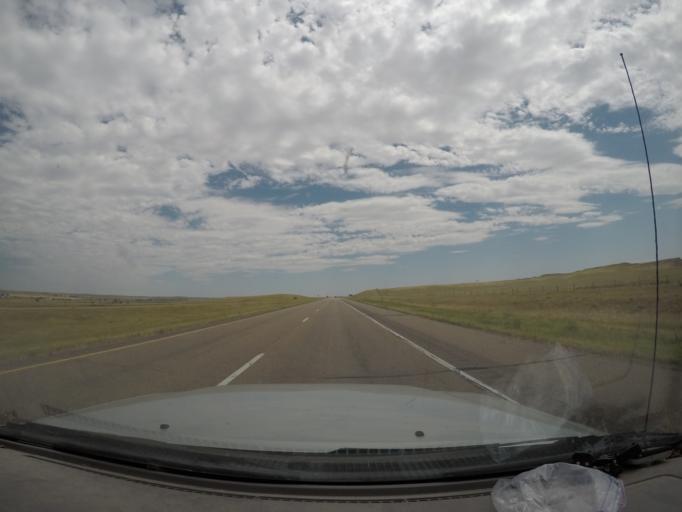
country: US
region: Nebraska
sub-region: Cheyenne County
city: Sidney
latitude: 41.1754
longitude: -103.1219
